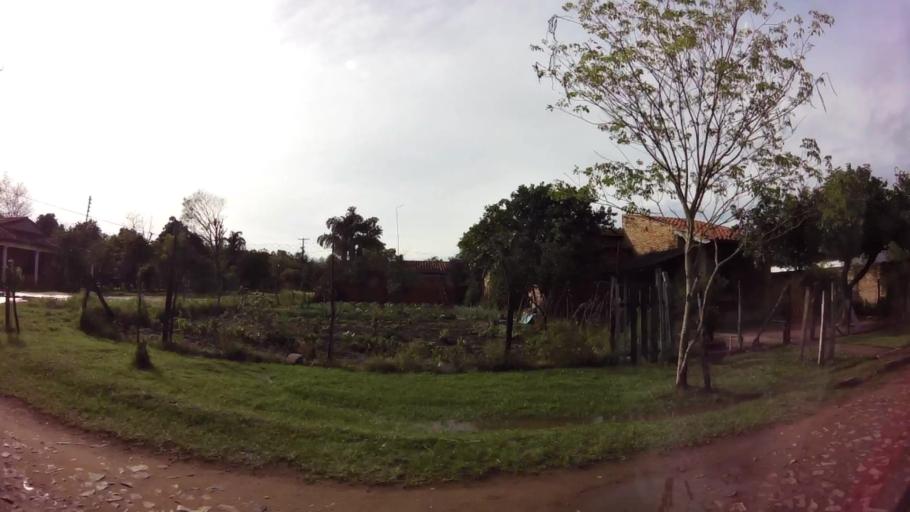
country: PY
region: Central
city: Limpio
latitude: -25.1875
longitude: -57.4827
